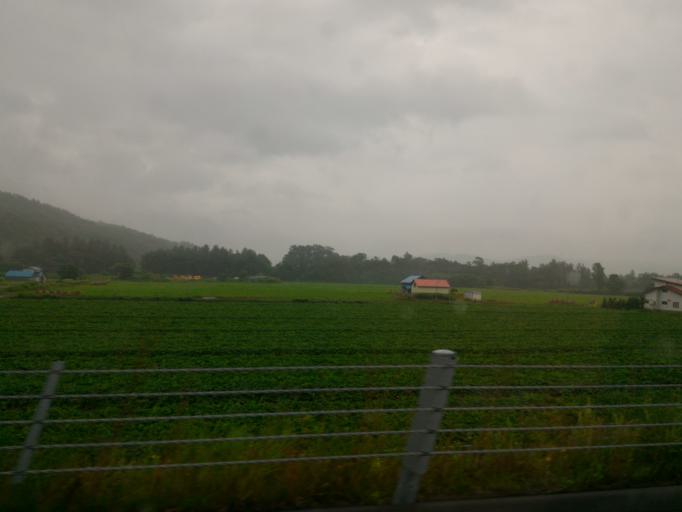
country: JP
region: Hokkaido
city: Nayoro
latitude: 44.4785
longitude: 142.3684
